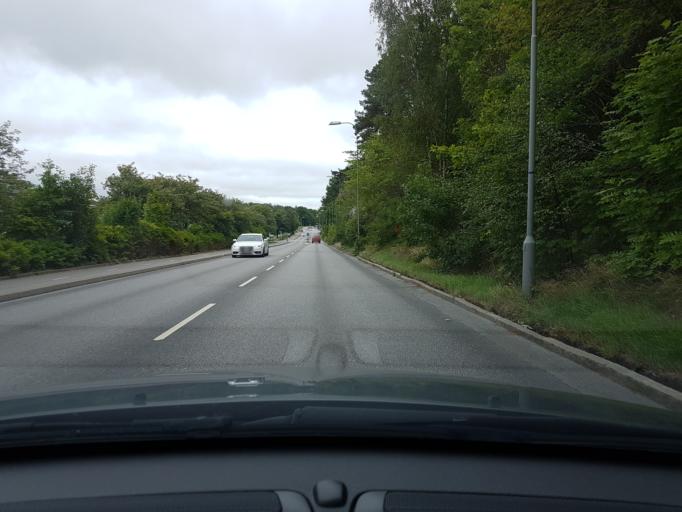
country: SE
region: Vaestra Goetaland
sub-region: Goteborg
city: Majorna
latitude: 57.6428
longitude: 11.8951
